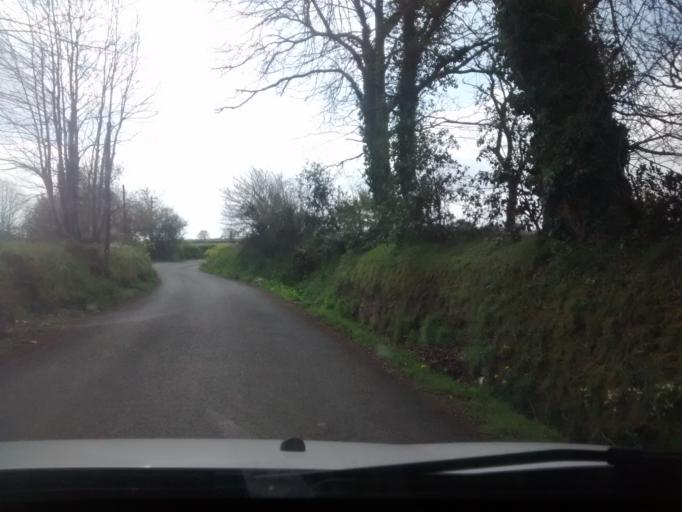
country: FR
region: Brittany
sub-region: Departement des Cotes-d'Armor
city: Penvenan
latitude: 48.8219
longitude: -3.3099
